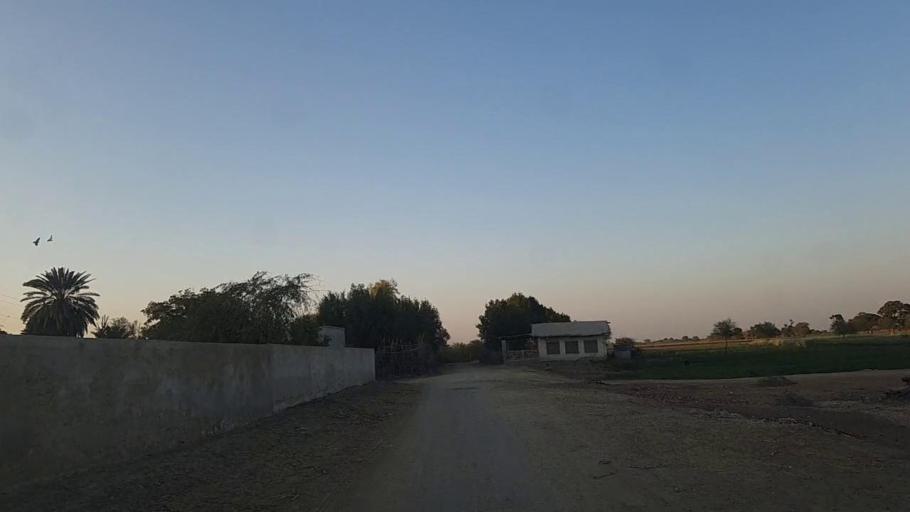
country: PK
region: Sindh
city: Naukot
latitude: 25.0381
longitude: 69.4101
